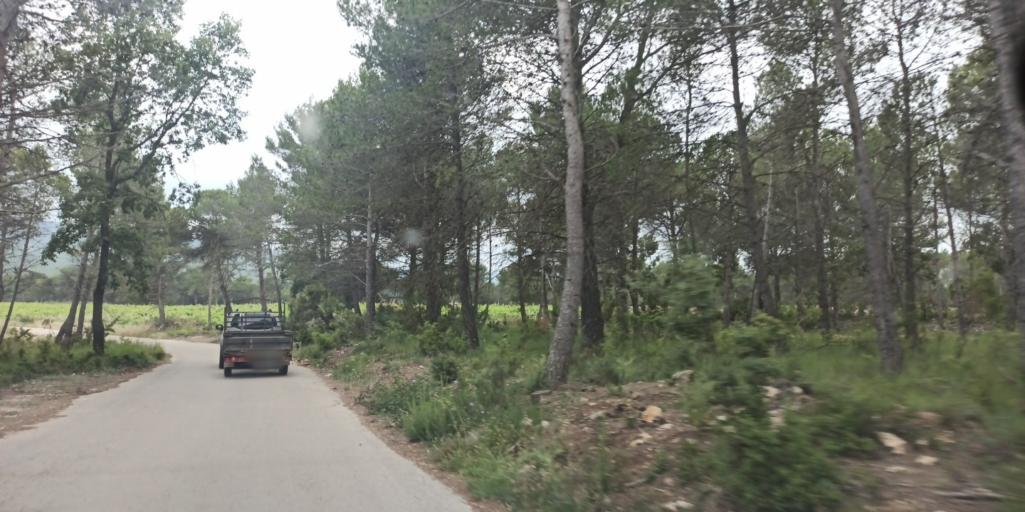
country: ES
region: Catalonia
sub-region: Provincia de Tarragona
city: Querol
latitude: 41.4257
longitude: 1.5002
